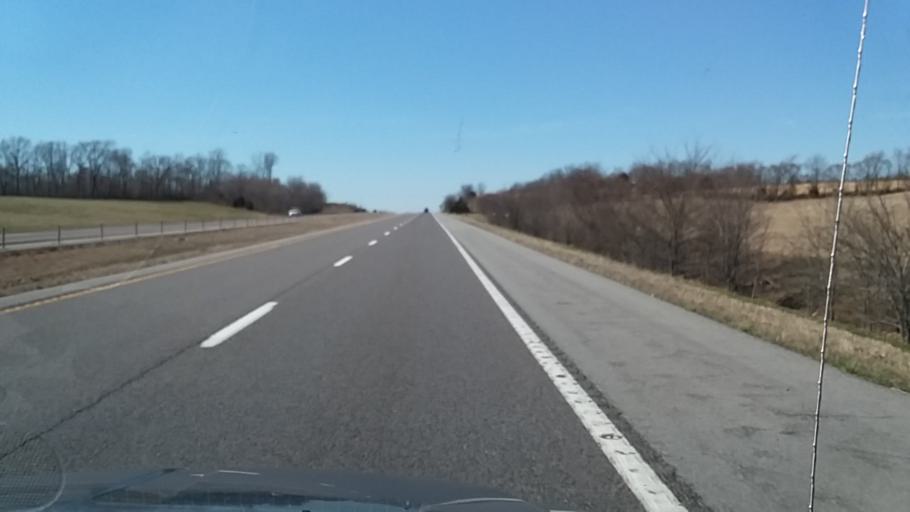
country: US
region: Missouri
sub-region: Cape Girardeau County
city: Jackson
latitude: 37.5206
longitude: -89.7030
